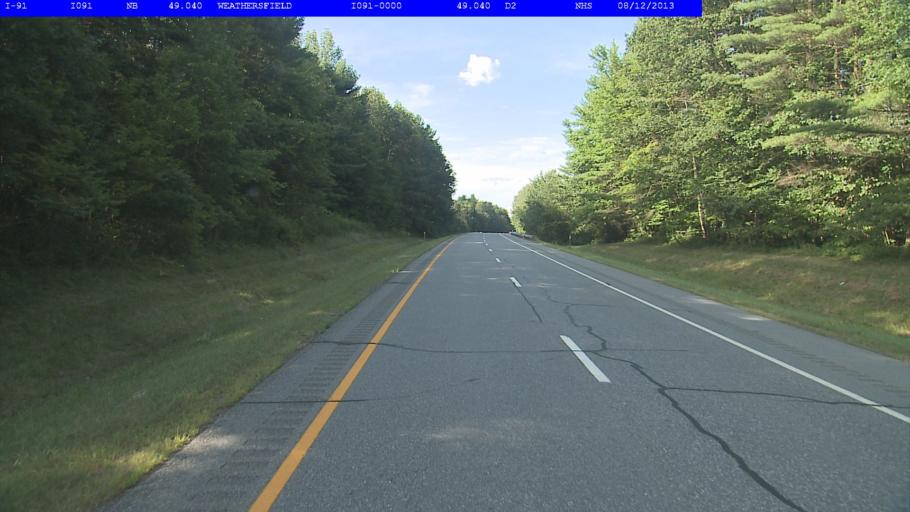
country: US
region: New Hampshire
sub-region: Sullivan County
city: Claremont
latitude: 43.3701
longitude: -72.4245
